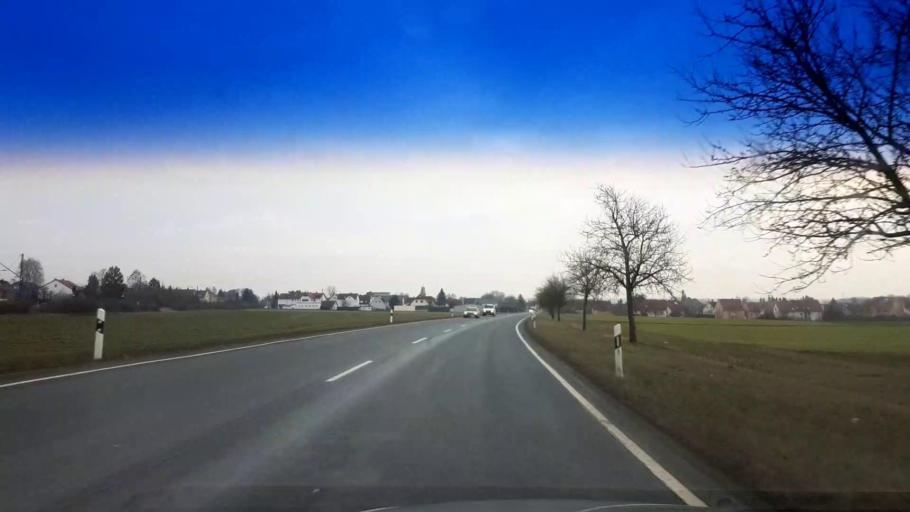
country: DE
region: Bavaria
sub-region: Upper Franconia
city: Altendorf
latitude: 49.8051
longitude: 11.0065
